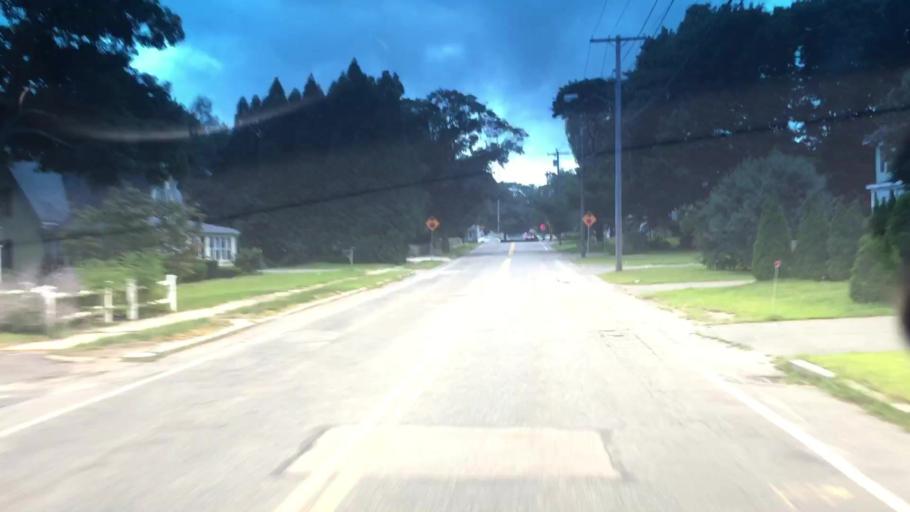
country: US
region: Massachusetts
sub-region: Norfolk County
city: Norwood
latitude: 42.1623
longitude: -71.2072
